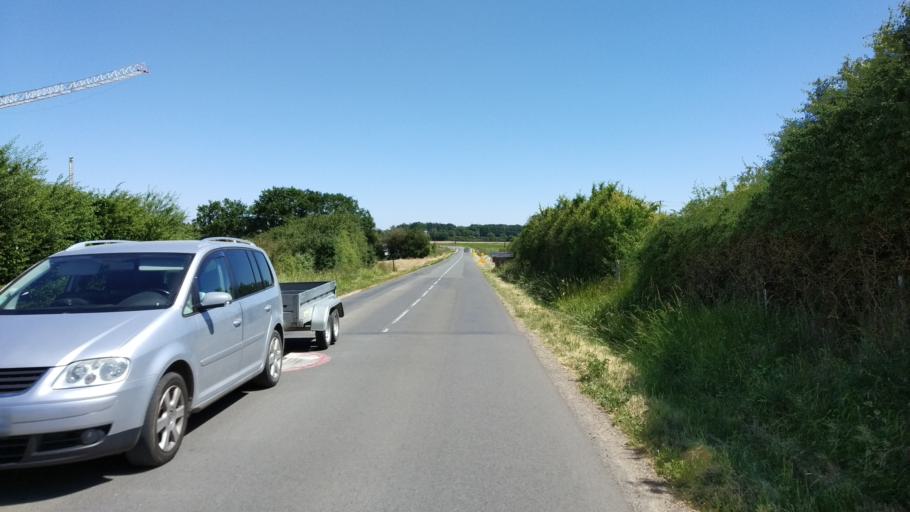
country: FR
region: Poitou-Charentes
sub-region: Departement de la Vienne
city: Biard
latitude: 46.6015
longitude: 0.2882
